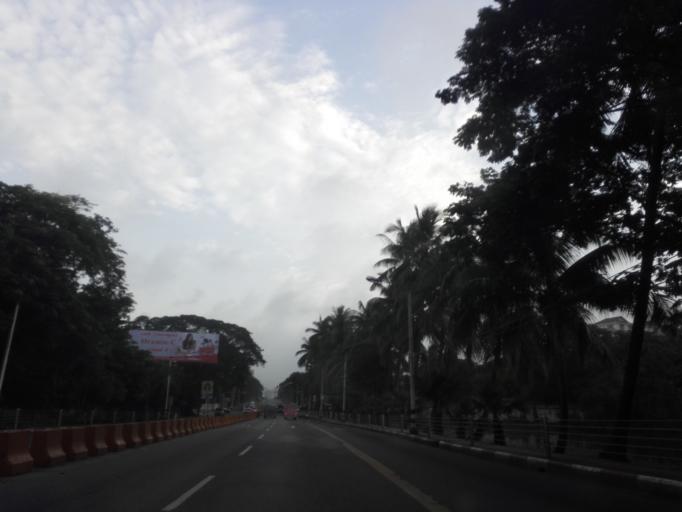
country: MM
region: Yangon
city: Yangon
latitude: 16.8518
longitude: 96.1405
